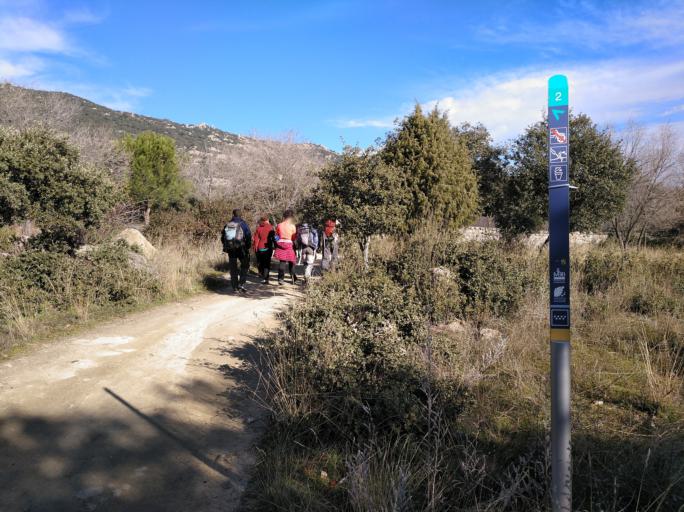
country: ES
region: Madrid
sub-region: Provincia de Madrid
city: Hoyo de Manzanares
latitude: 40.6255
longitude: -3.9152
